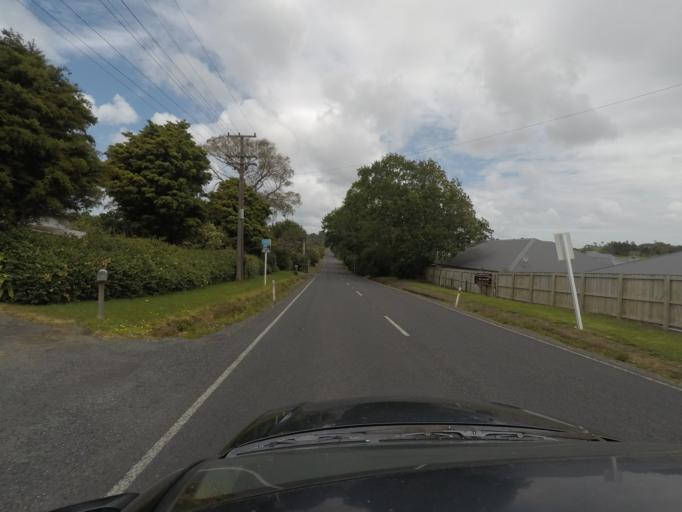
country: NZ
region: Auckland
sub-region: Auckland
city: Parakai
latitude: -36.6276
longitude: 174.5020
